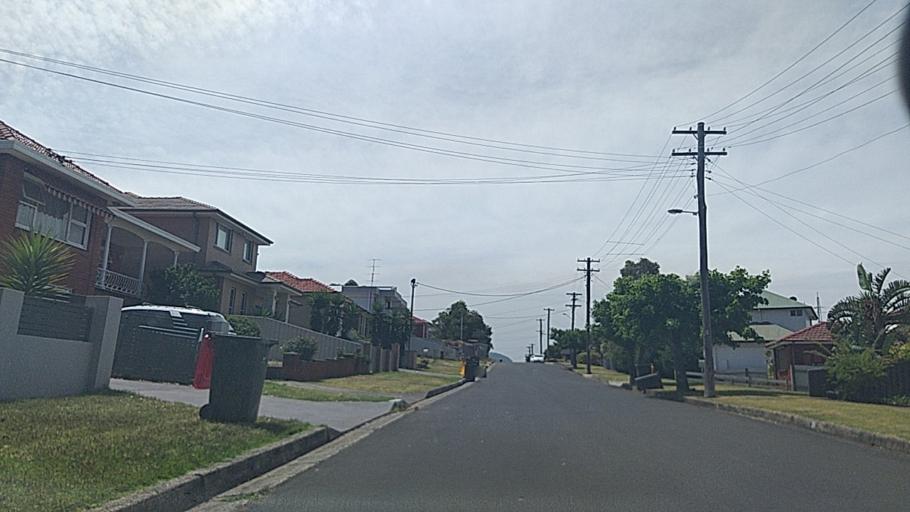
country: AU
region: New South Wales
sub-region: Wollongong
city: Mount Ousley
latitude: -34.3934
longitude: 150.8825
